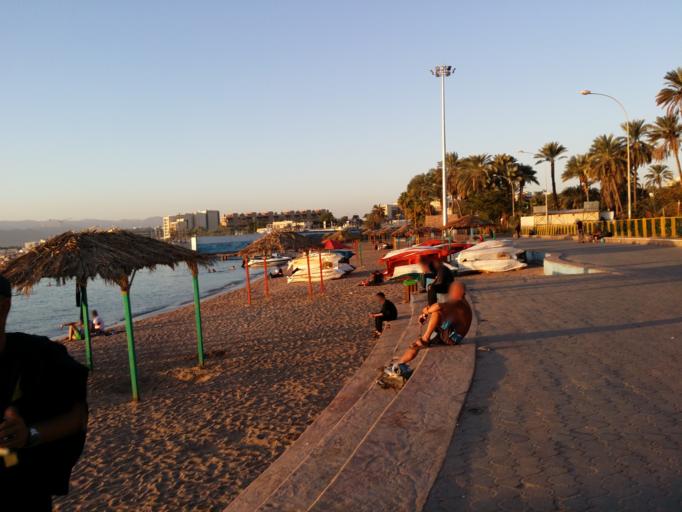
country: JO
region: Aqaba
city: Aqaba
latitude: 29.5261
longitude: 35.0009
